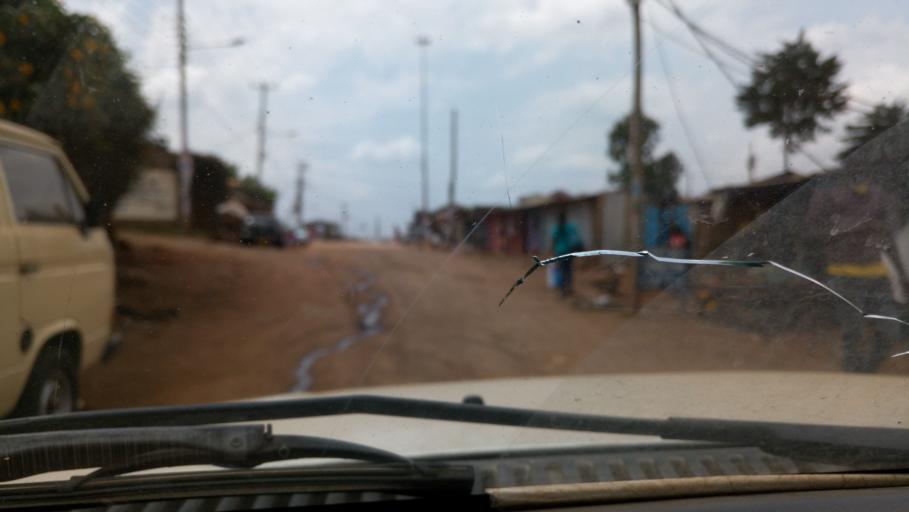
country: KE
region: Nairobi Area
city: Nairobi
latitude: -1.2759
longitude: 36.7399
